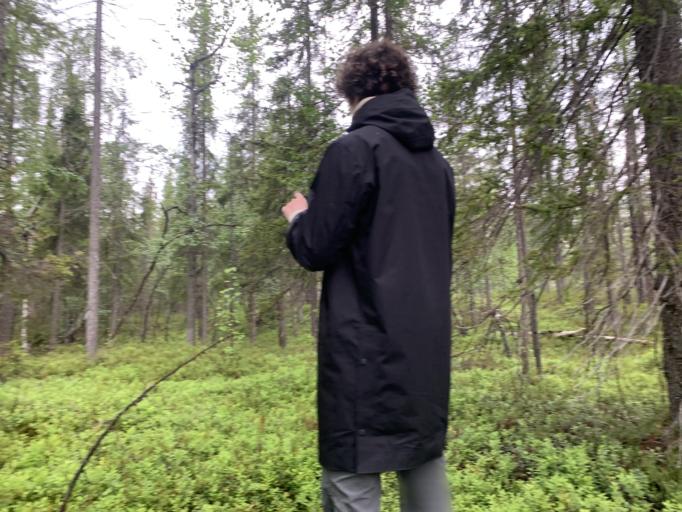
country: RU
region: Murmansk
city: Afrikanda
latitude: 67.6597
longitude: 32.9134
